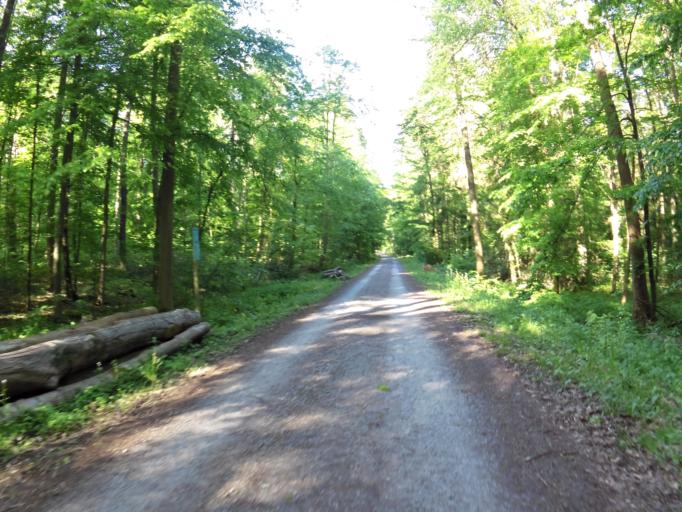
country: DE
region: Bavaria
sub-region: Regierungsbezirk Unterfranken
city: Reichenberg
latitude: 49.7521
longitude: 9.9079
